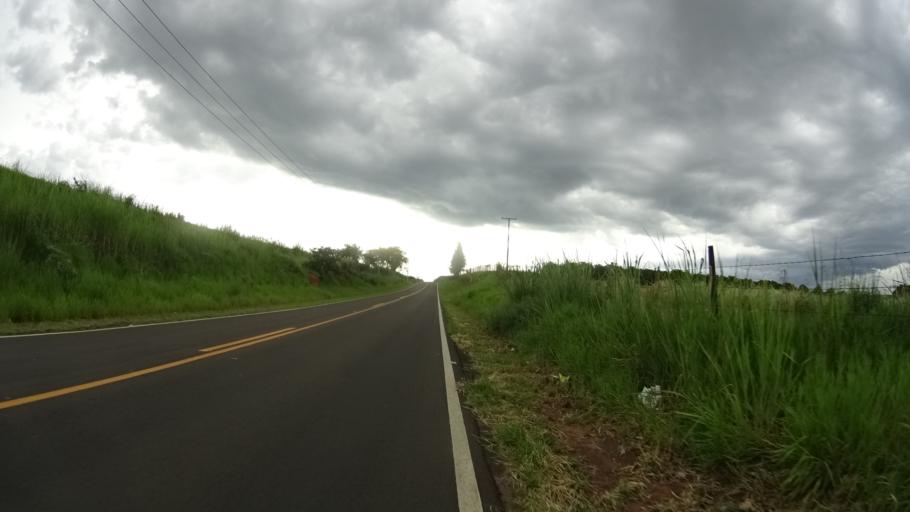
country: BR
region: Sao Paulo
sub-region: Marilia
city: Marilia
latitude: -22.2147
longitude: -49.8325
